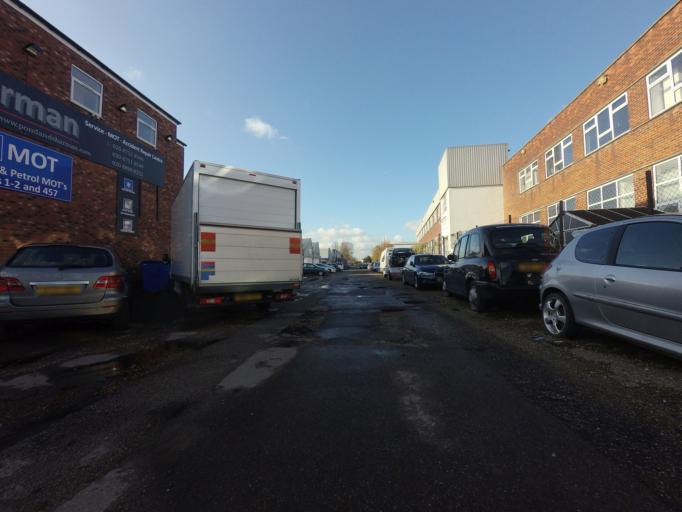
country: GB
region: England
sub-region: Greater London
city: Feltham
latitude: 51.4427
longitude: -0.4062
